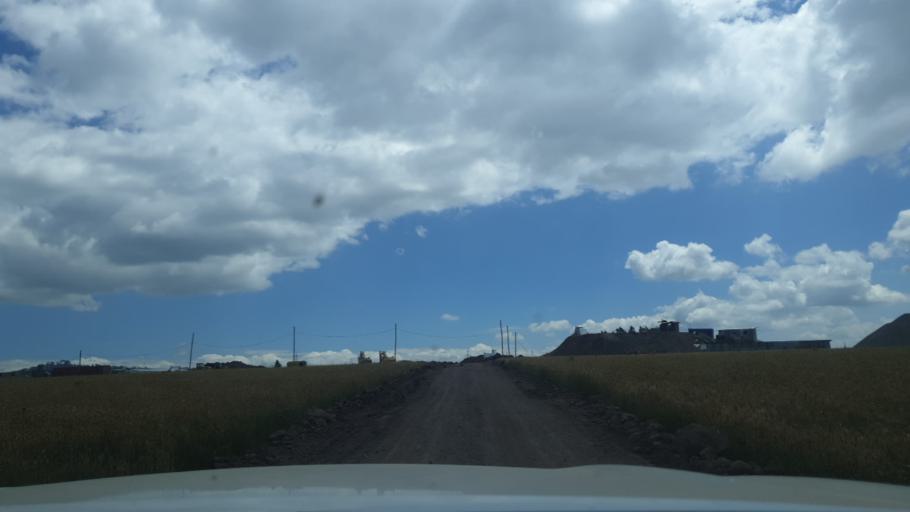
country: ET
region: Oromiya
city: Huruta
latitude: 7.8314
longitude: 39.1189
